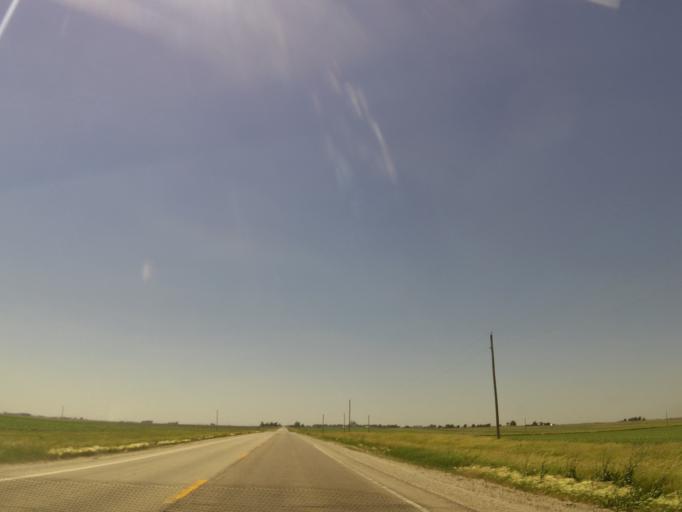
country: US
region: Illinois
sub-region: Livingston County
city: Fairbury
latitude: 40.7432
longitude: -88.5806
